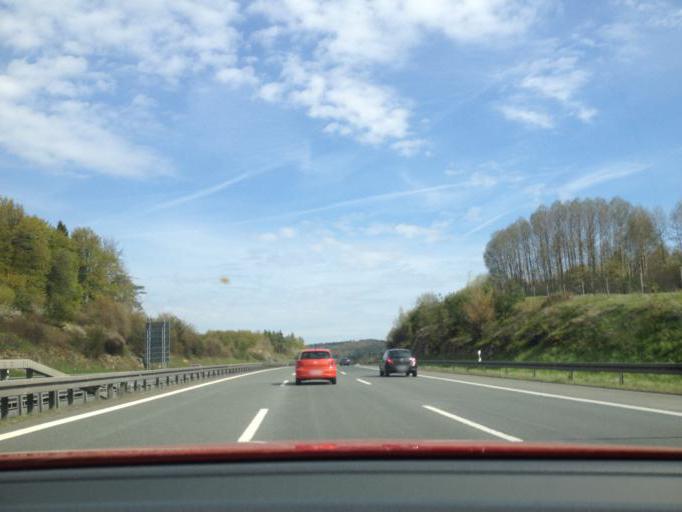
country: DE
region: Bavaria
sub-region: Upper Franconia
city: Pegnitz
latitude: 49.7565
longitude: 11.5095
